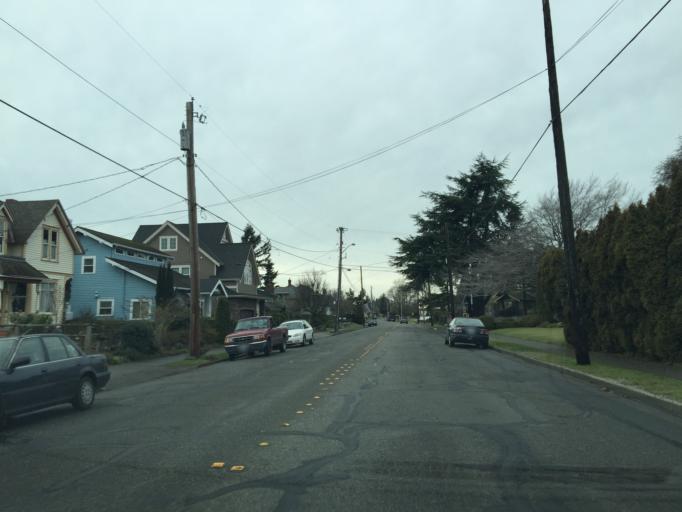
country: US
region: Washington
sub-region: Whatcom County
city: Bellingham
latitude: 48.7602
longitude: -122.5000
